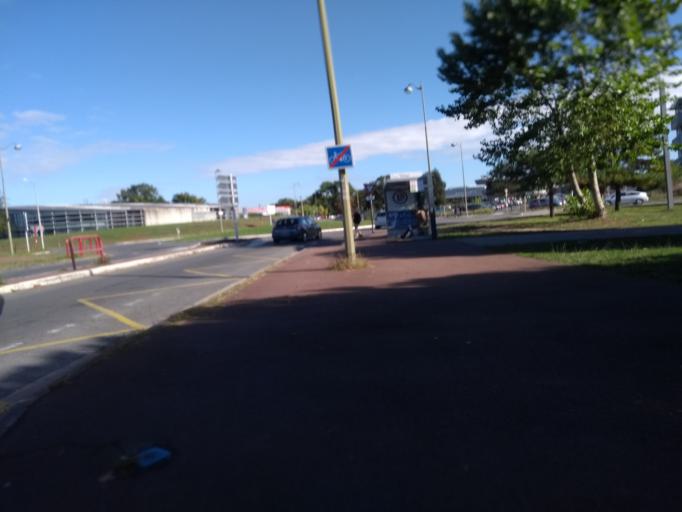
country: FR
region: Aquitaine
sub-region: Departement de la Gironde
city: Pessac
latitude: 44.7965
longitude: -0.6215
